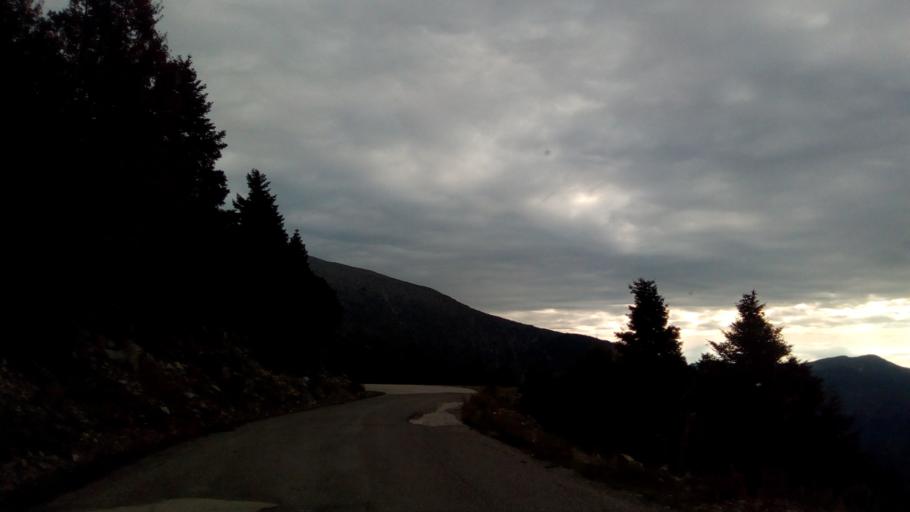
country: GR
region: West Greece
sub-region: Nomos Aitolias kai Akarnanias
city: Thermo
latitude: 38.6235
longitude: 21.8221
